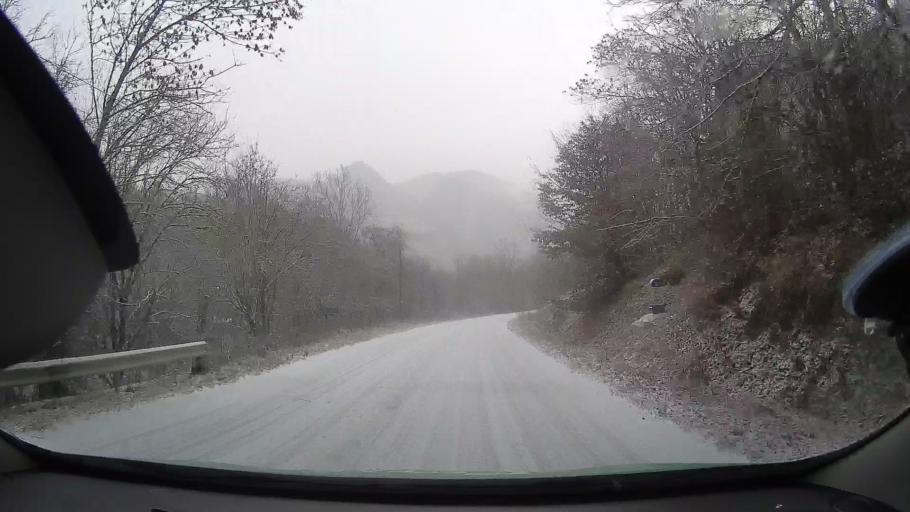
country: RO
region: Alba
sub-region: Comuna Rimetea
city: Rimetea
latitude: 46.3852
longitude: 23.5769
